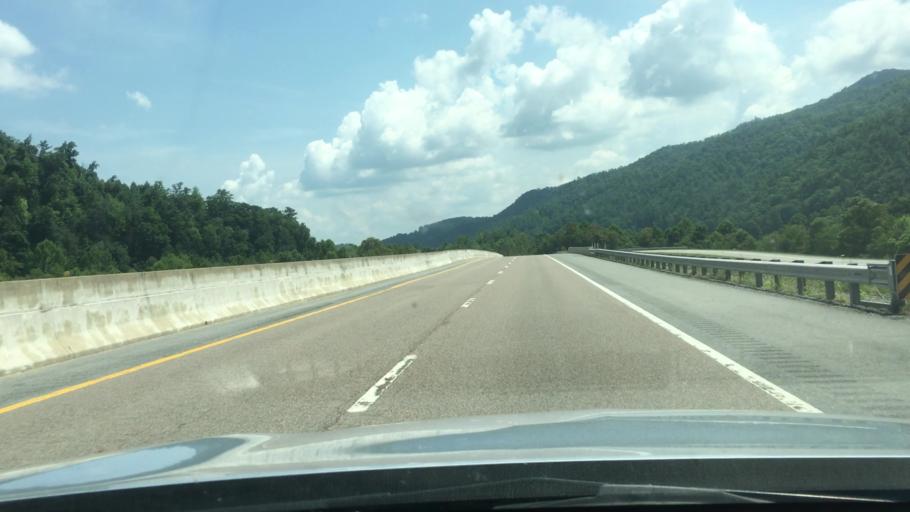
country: US
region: Tennessee
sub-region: Unicoi County
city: Banner Hill
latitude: 36.0861
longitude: -82.4917
